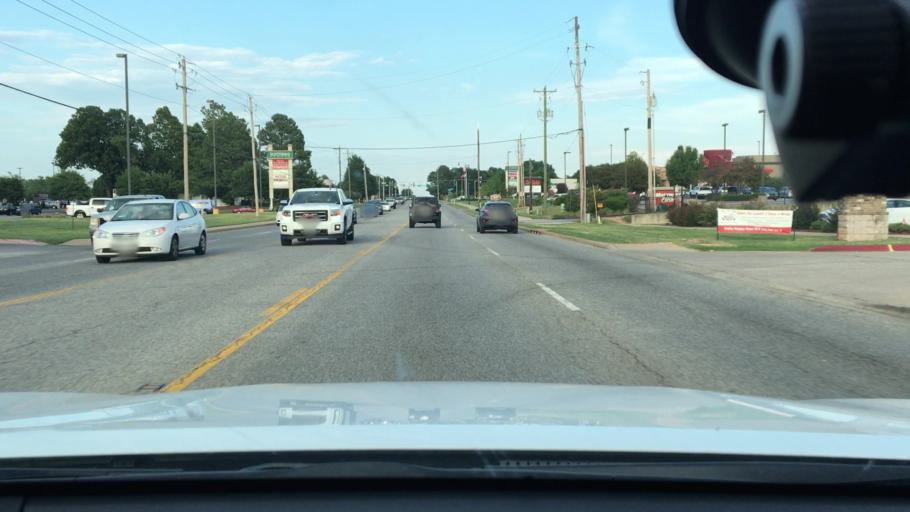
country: US
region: Arkansas
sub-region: Benton County
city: Bentonville
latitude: 36.3349
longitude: -94.1790
